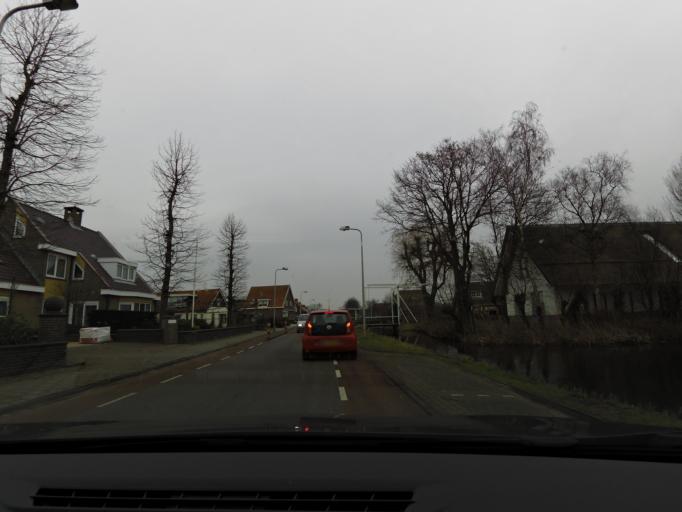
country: NL
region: South Holland
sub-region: Gemeente Nieuwkoop
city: Nieuwkoop
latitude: 52.1631
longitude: 4.8175
